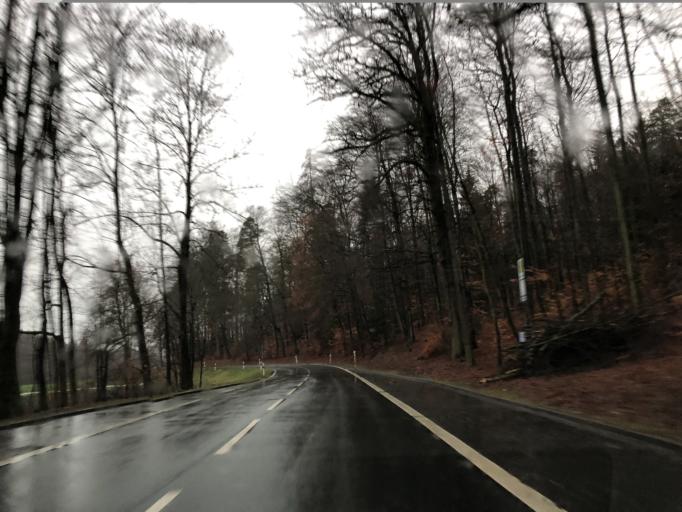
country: DE
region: Hesse
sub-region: Regierungsbezirk Darmstadt
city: Bad Konig
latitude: 49.7364
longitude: 9.0426
